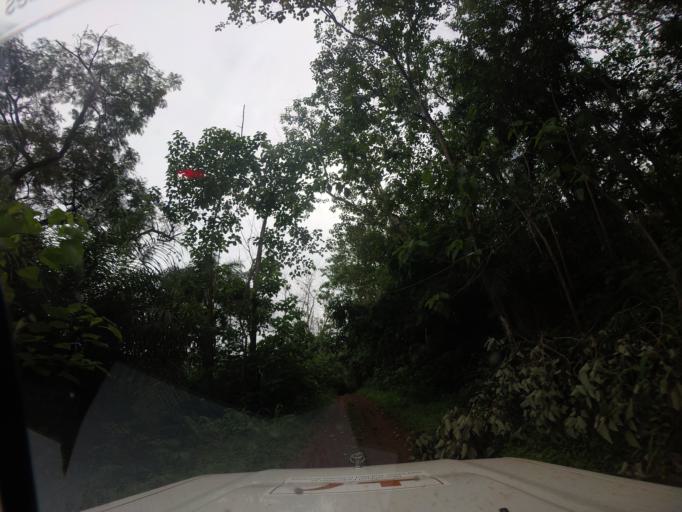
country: SL
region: Northern Province
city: Kamakwie
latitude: 9.6414
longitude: -12.2157
